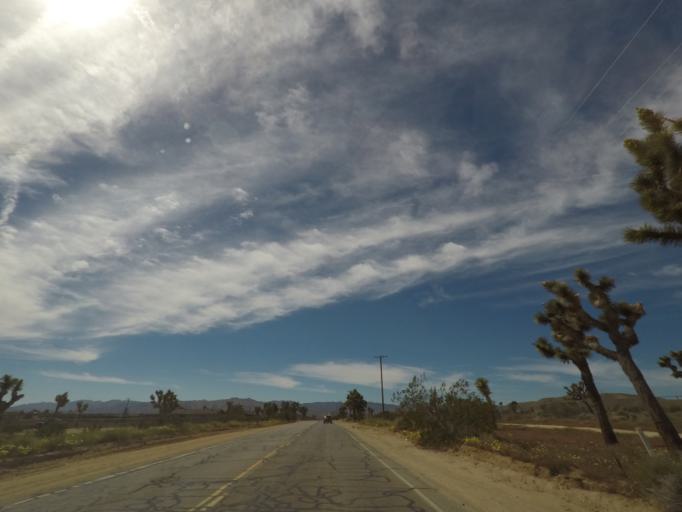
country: US
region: California
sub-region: San Bernardino County
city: Joshua Tree
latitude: 34.1748
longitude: -116.3696
